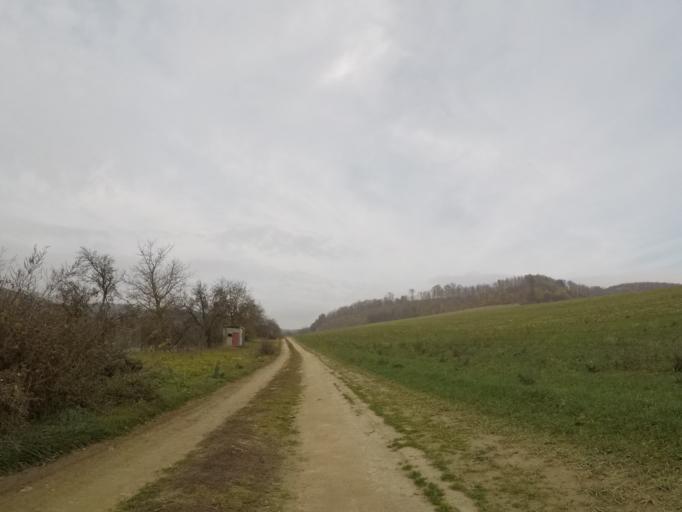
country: SK
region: Presovsky
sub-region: Okres Presov
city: Presov
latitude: 48.9157
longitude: 21.1455
